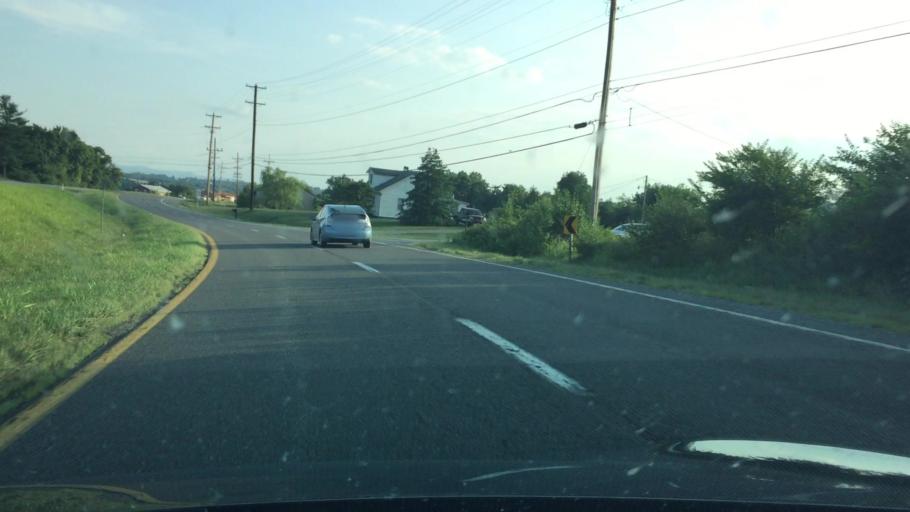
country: US
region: Virginia
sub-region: Pulaski County
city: Fairlawn
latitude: 37.1447
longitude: -80.6032
